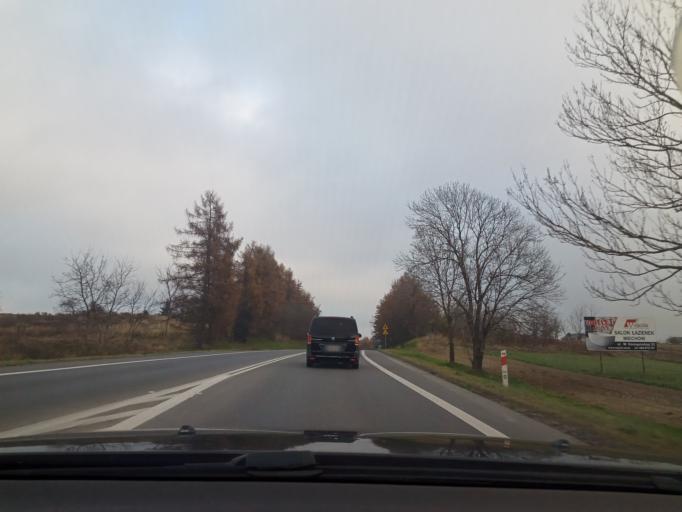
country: PL
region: Lesser Poland Voivodeship
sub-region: Powiat miechowski
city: Miechow
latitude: 50.3474
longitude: 20.0374
